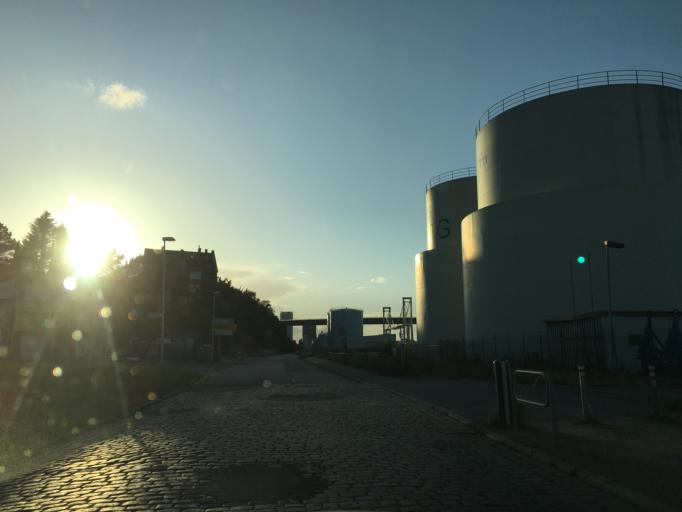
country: DE
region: Schleswig-Holstein
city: Altenholz
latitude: 54.3658
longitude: 10.1327
